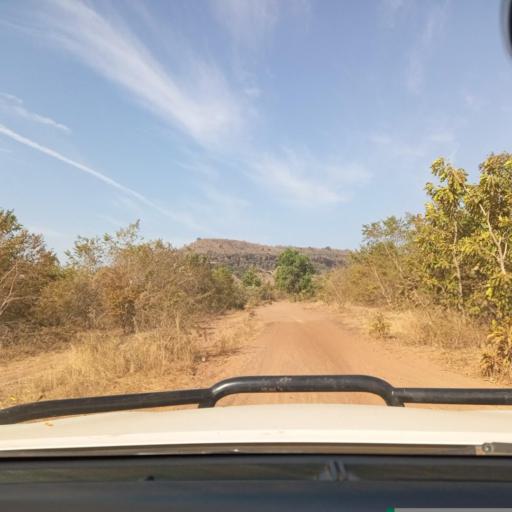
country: ML
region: Bamako
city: Bamako
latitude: 12.5561
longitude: -8.1455
